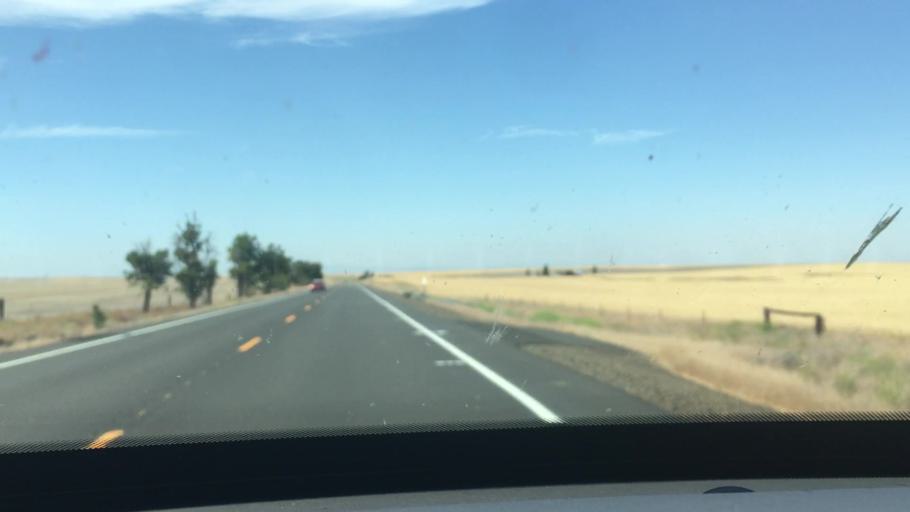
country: US
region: Oregon
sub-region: Sherman County
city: Moro
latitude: 45.3197
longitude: -120.7686
